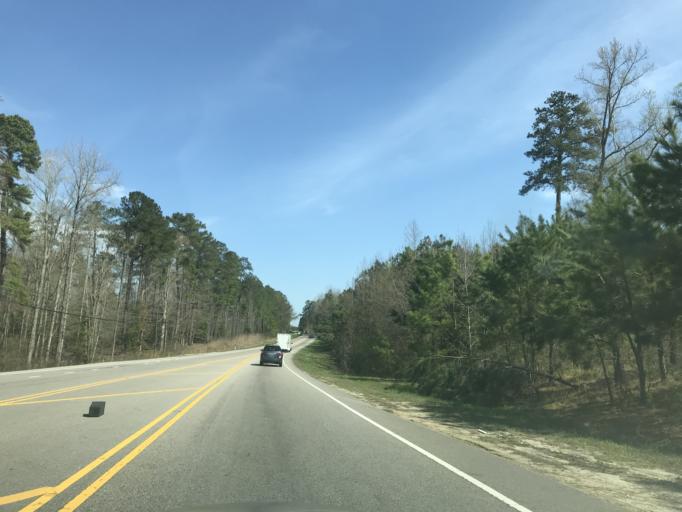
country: US
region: North Carolina
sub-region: Wake County
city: Knightdale
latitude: 35.8461
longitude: -78.5206
